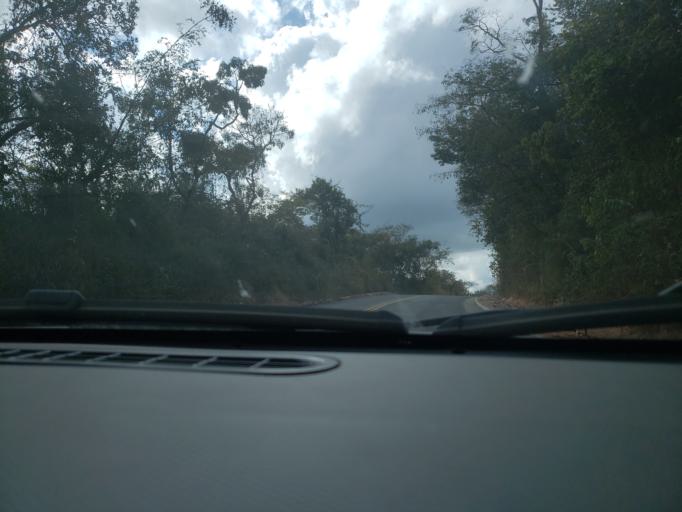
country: BR
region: Minas Gerais
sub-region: Campo Belo
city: Campo Belo
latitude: -20.9165
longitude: -45.2940
